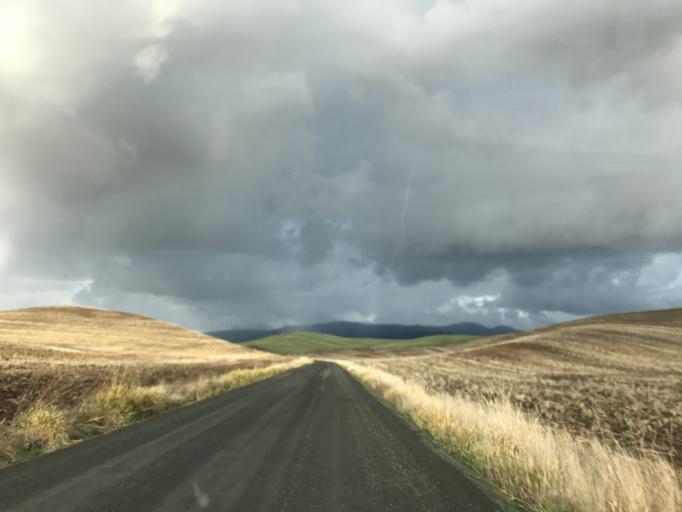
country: US
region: Idaho
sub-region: Latah County
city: Moscow
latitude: 46.7593
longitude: -116.9943
